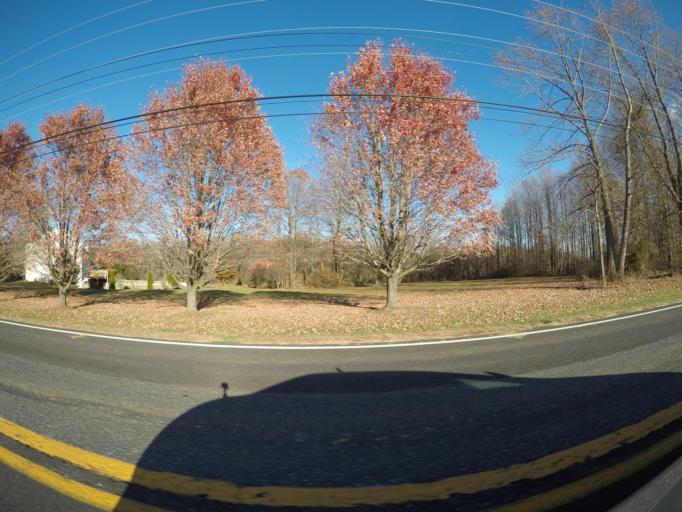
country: US
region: Maryland
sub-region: Harford County
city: South Bel Air
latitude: 39.6247
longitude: -76.2610
